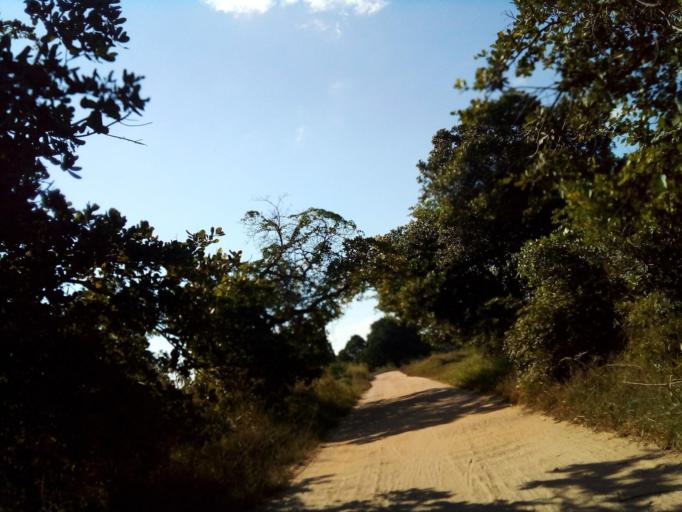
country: MZ
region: Zambezia
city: Quelimane
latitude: -17.5264
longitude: 36.6165
